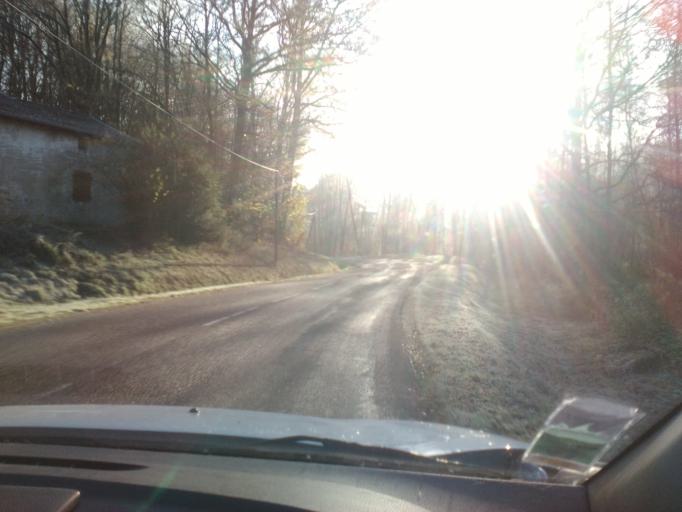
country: FR
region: Lorraine
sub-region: Departement des Vosges
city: Uzemain
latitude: 48.0609
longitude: 6.3382
